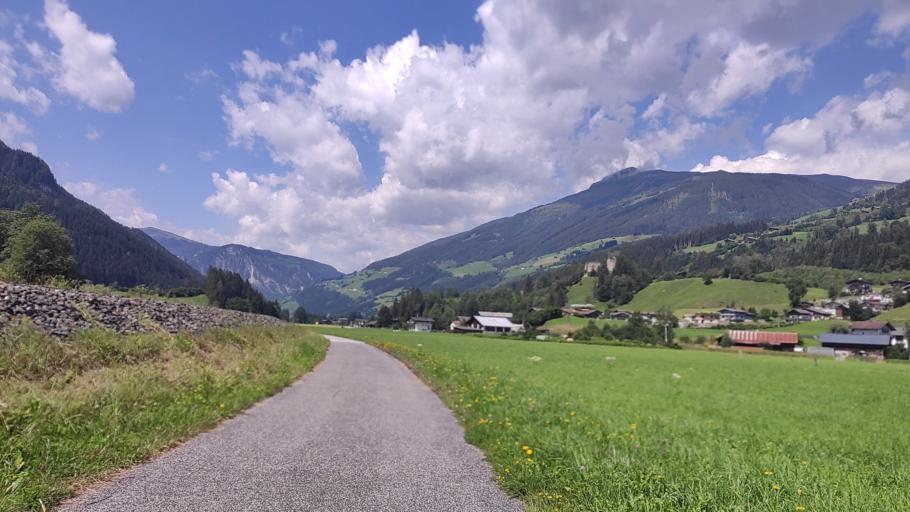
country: AT
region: Salzburg
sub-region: Politischer Bezirk Zell am See
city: Wald im Pinzgau
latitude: 47.2444
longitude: 12.2531
